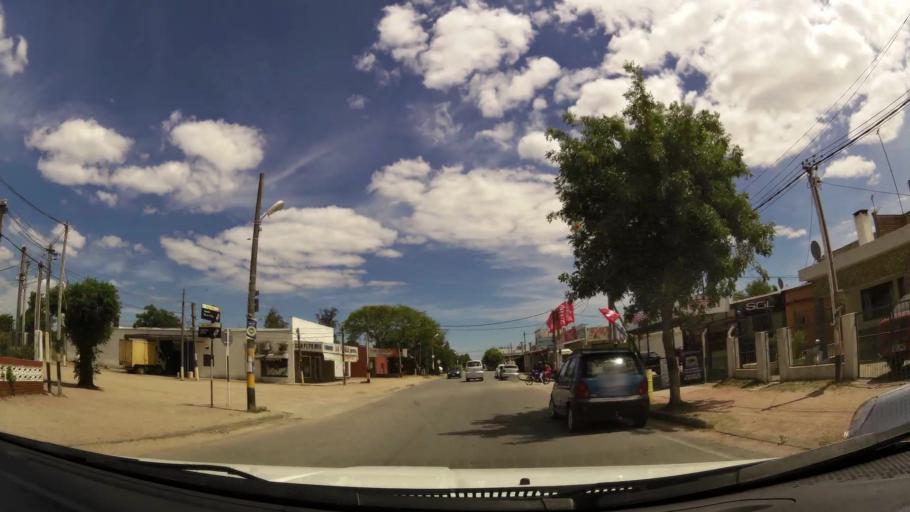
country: UY
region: San Jose
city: Delta del Tigre
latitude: -34.7483
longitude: -56.4544
